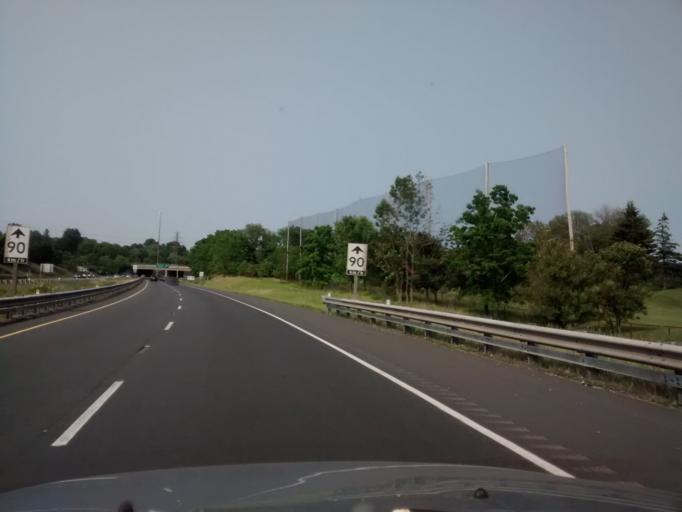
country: CA
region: Ontario
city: Hamilton
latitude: 43.2495
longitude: -79.9172
